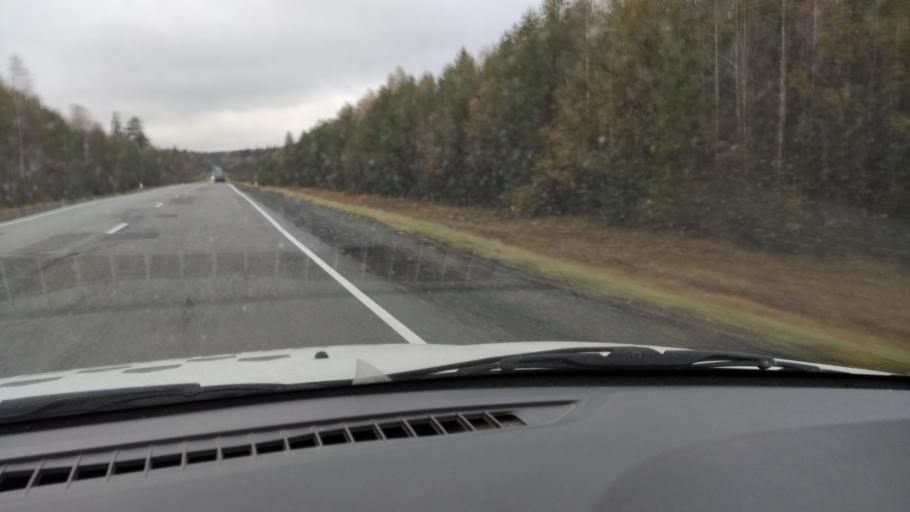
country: RU
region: Kirov
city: Dubrovka
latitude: 58.9046
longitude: 51.2726
